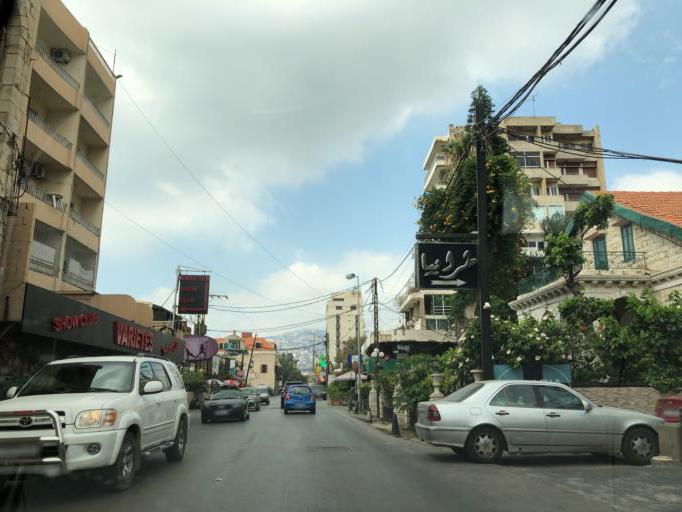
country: LB
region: Mont-Liban
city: Djounie
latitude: 33.9896
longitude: 35.6384
